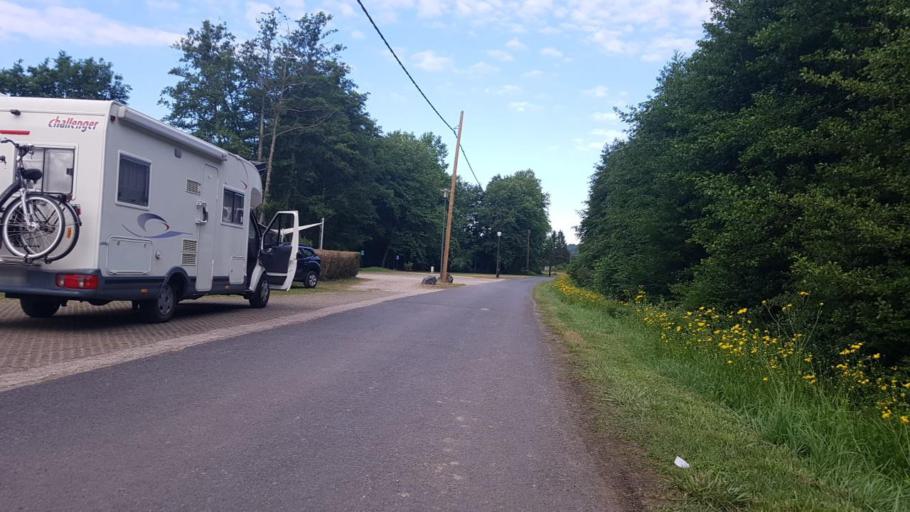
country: FR
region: Lorraine
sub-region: Departement de Meurthe-et-Moselle
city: Gondreville
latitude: 48.6538
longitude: 5.9912
